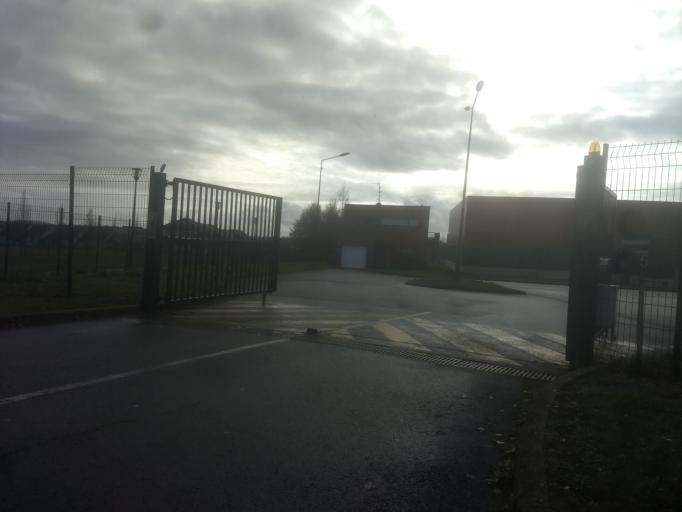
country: FR
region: Nord-Pas-de-Calais
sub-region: Departement du Pas-de-Calais
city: Dainville
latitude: 50.2909
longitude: 2.7322
